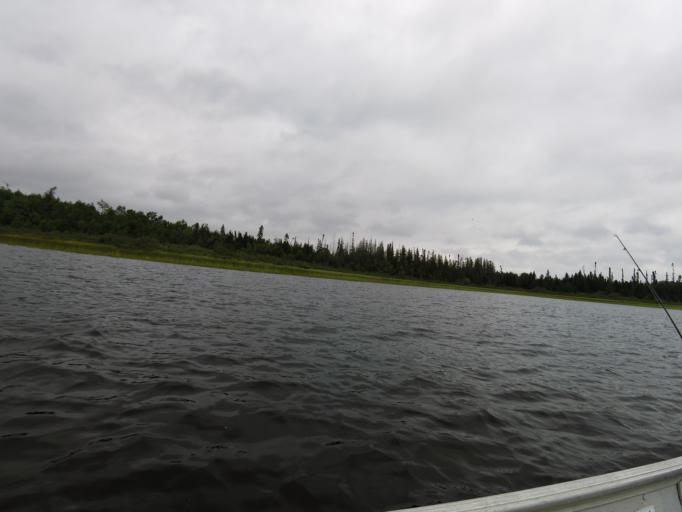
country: CA
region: Ontario
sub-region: Rainy River District
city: Atikokan
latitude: 49.5987
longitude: -91.3452
